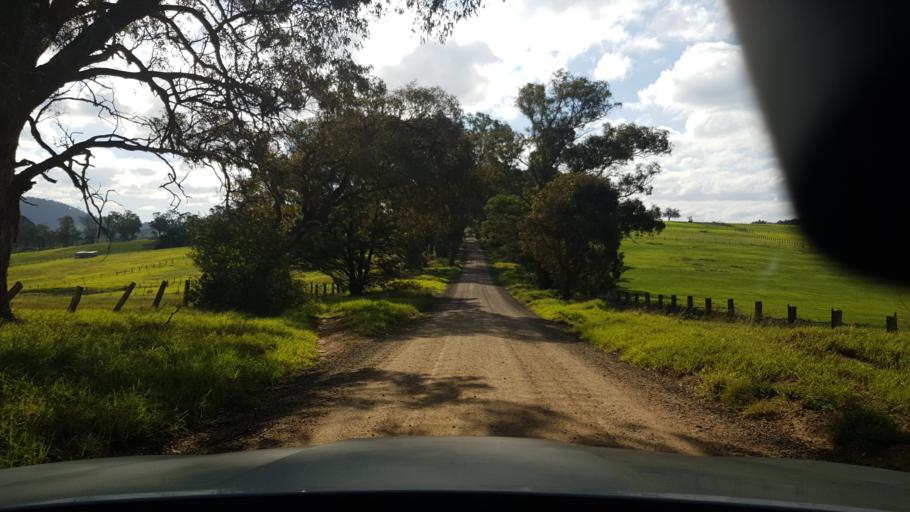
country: AU
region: Victoria
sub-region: East Gippsland
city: Bairnsdale
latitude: -37.7812
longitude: 147.5749
